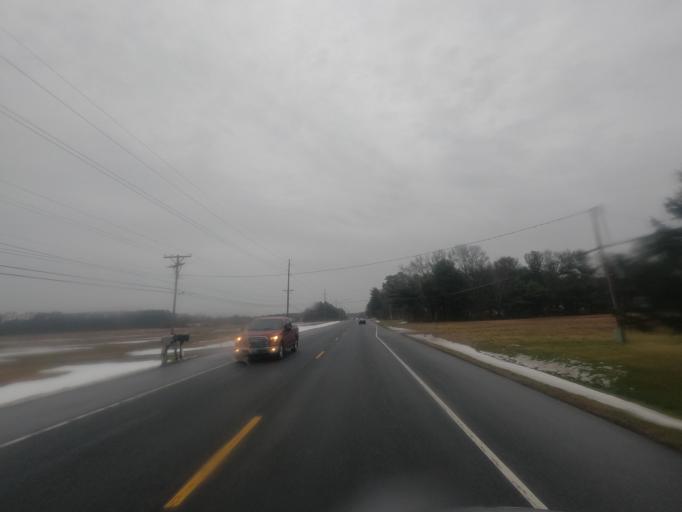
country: US
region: Maryland
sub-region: Dorchester County
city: Cambridge
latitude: 38.5589
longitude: -75.9984
